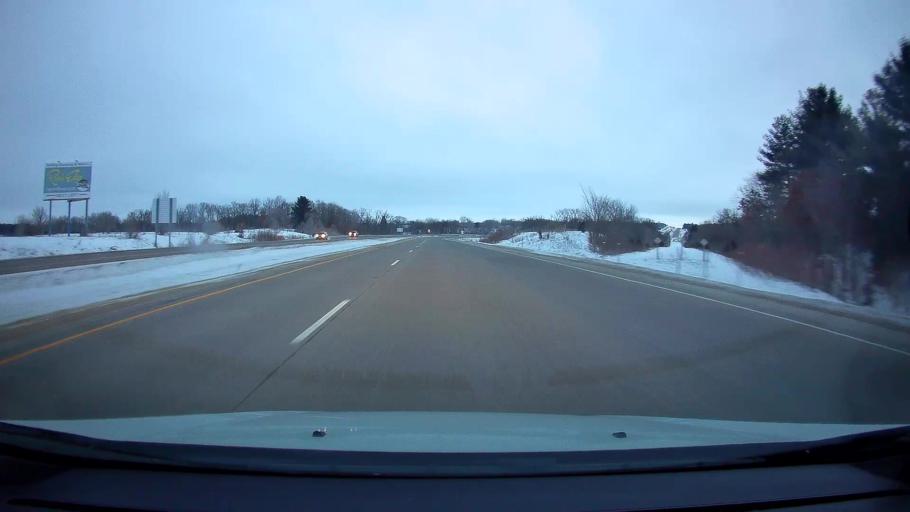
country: US
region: Wisconsin
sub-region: Saint Croix County
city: Somerset
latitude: 45.1224
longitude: -92.6484
